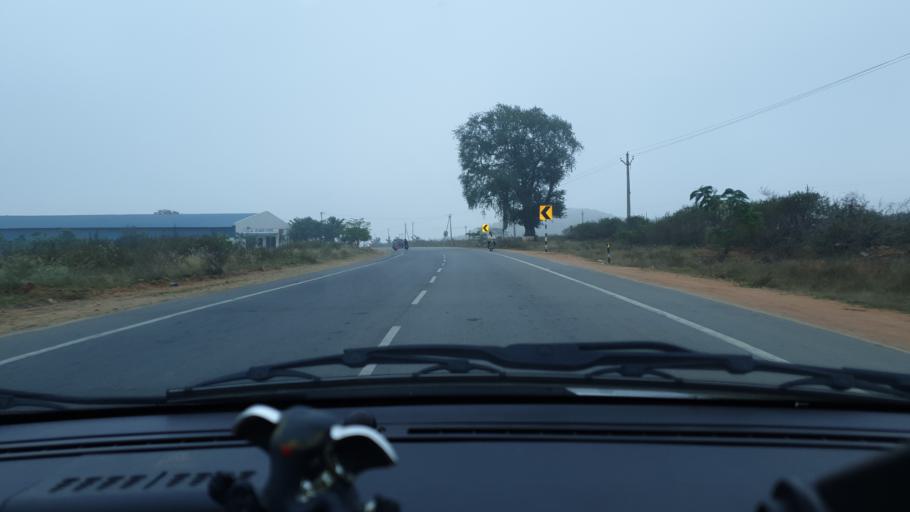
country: IN
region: Telangana
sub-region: Mahbubnagar
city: Farrukhnagar
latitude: 16.9455
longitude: 78.5244
